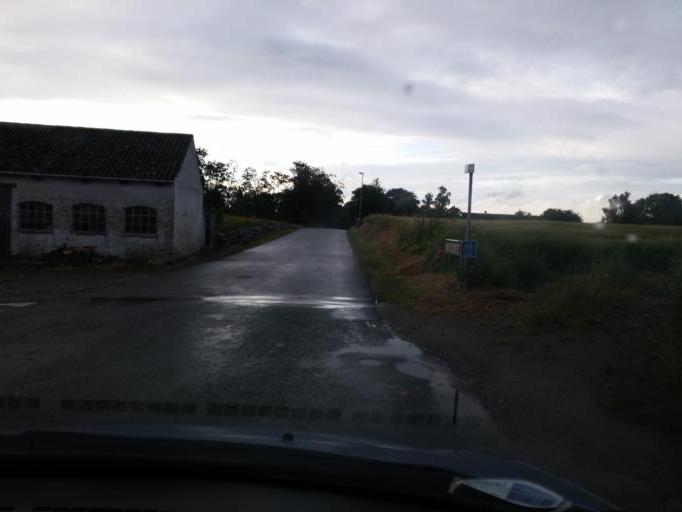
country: DK
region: South Denmark
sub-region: Kerteminde Kommune
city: Kerteminde
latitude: 55.5117
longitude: 10.6162
